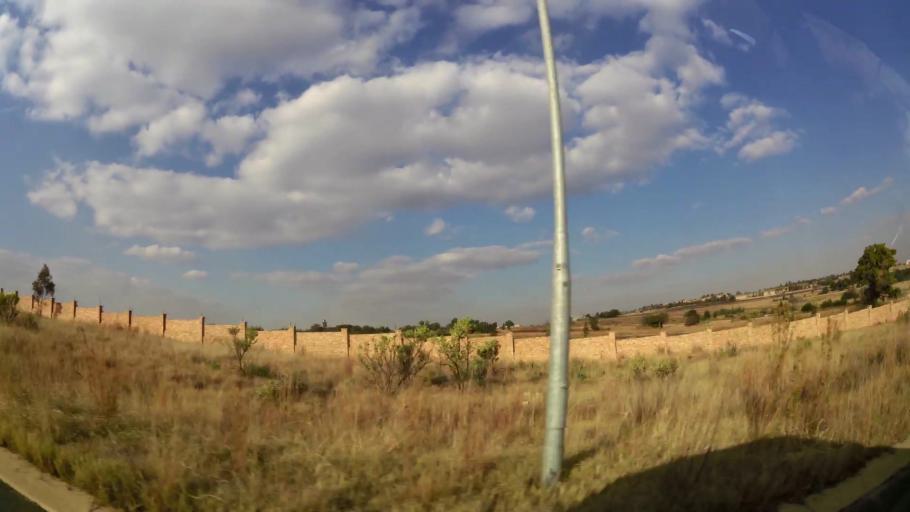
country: ZA
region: Gauteng
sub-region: West Rand District Municipality
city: Krugersdorp
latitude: -26.1027
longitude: 27.7326
